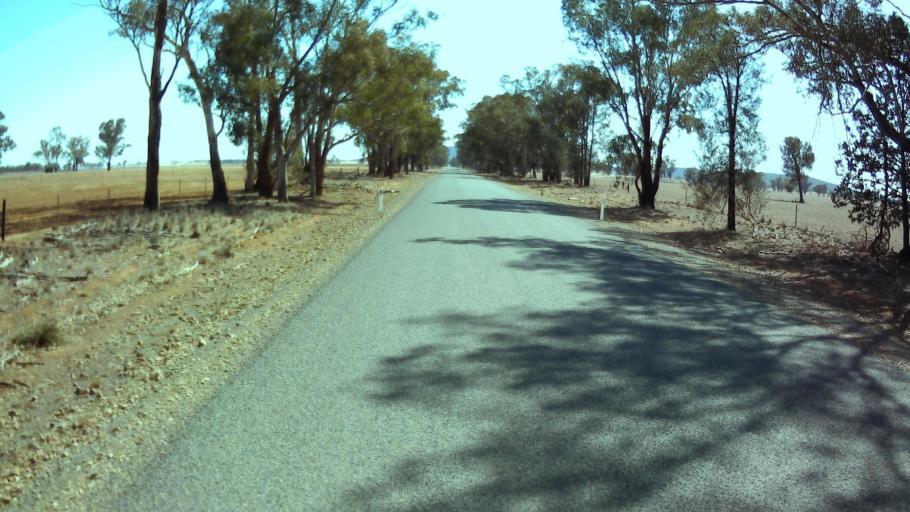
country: AU
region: New South Wales
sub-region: Weddin
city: Grenfell
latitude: -33.7184
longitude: 147.9026
